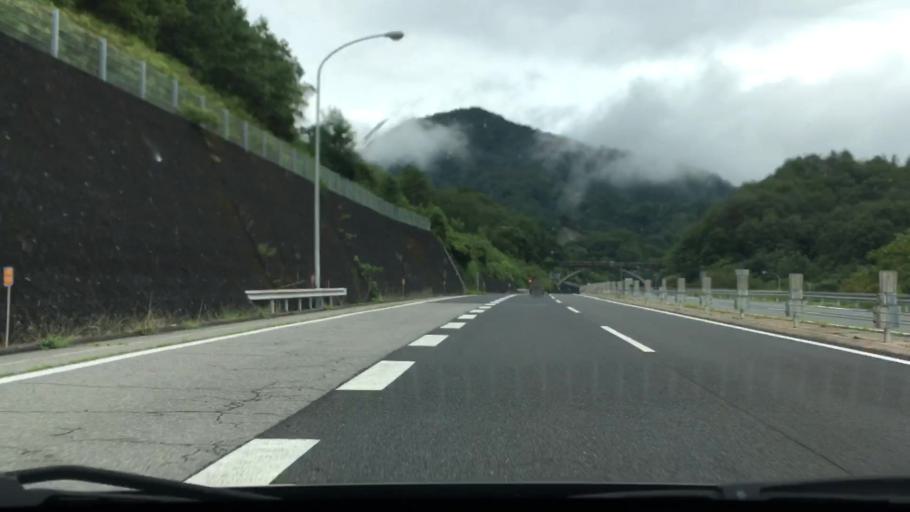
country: JP
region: Hiroshima
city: Hiroshima-shi
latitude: 34.5499
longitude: 132.4520
